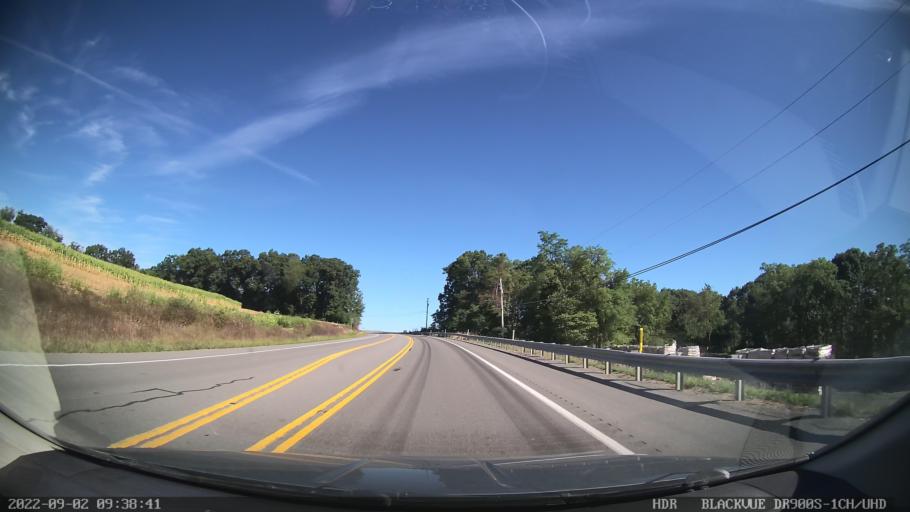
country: US
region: Pennsylvania
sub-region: Northumberland County
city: Elysburg
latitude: 40.9031
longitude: -76.5791
